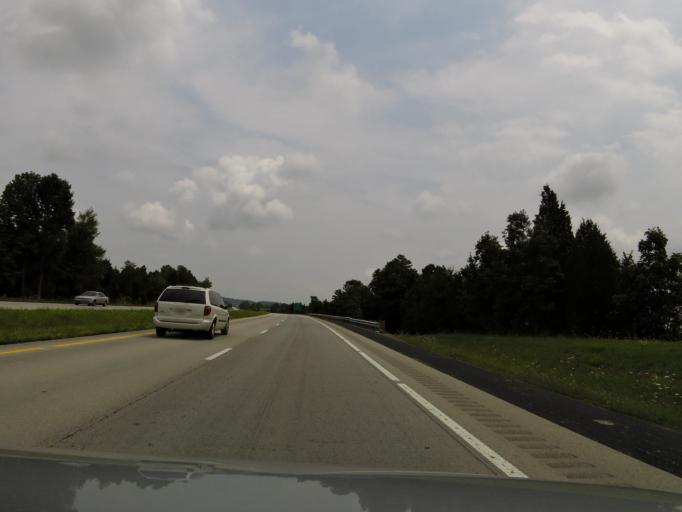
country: US
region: Kentucky
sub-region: Hardin County
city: Elizabethtown
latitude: 37.5639
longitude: -86.0553
